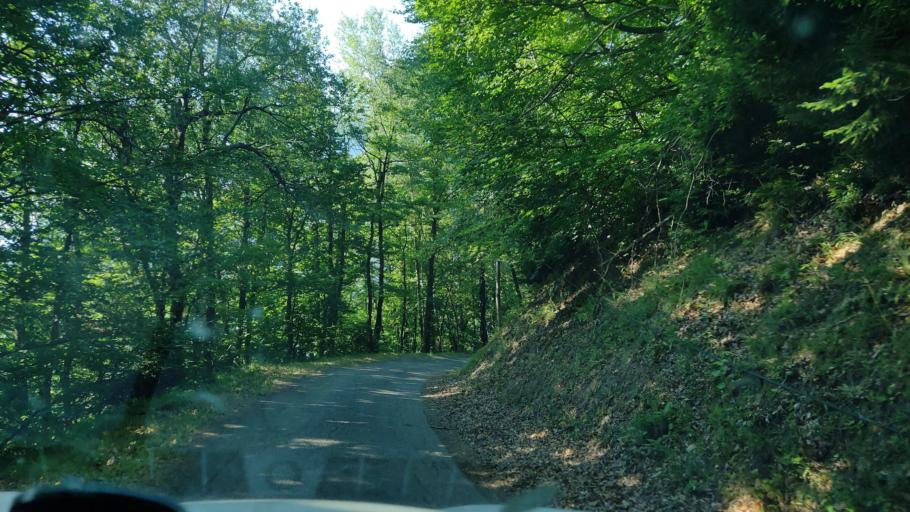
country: FR
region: Rhone-Alpes
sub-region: Departement de la Savoie
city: Saint-Etienne-de-Cuines
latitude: 45.3443
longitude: 6.2752
